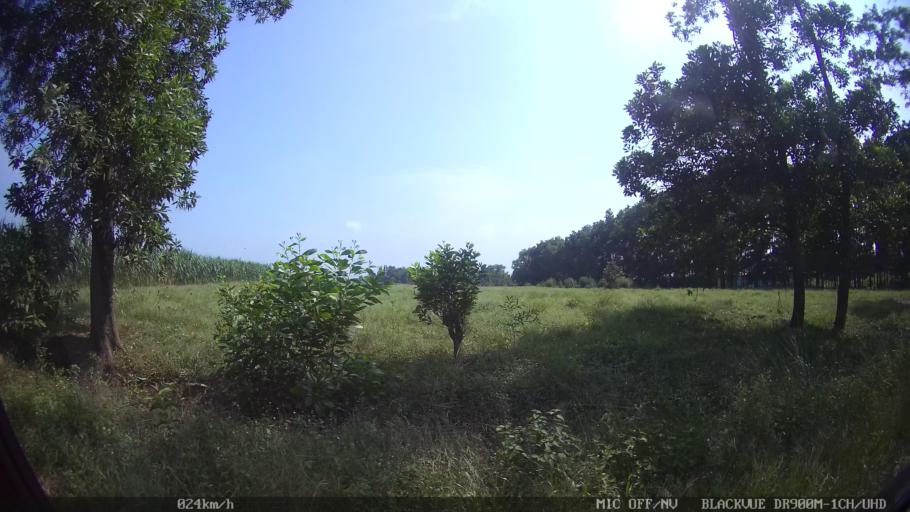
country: ID
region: Lampung
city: Natar
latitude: -5.2540
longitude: 105.2039
